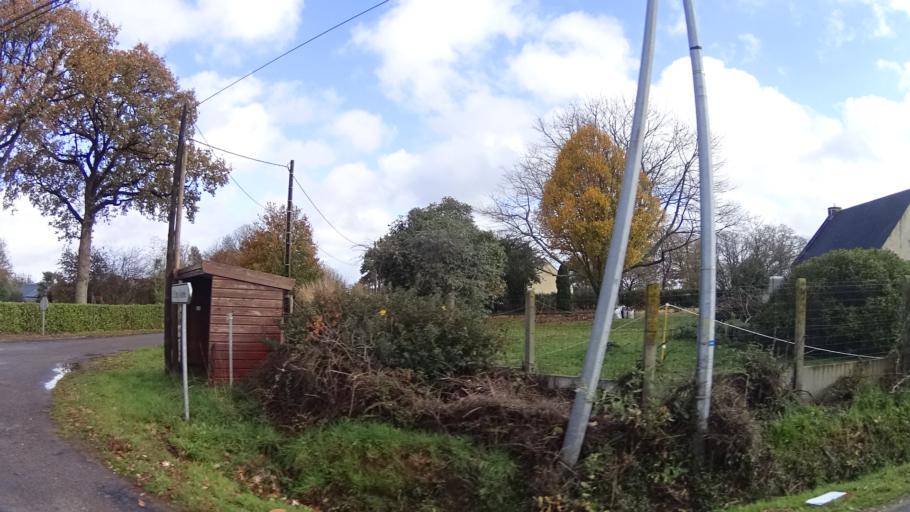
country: FR
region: Pays de la Loire
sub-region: Departement de la Loire-Atlantique
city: Saint-Nicolas-de-Redon
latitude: 47.6131
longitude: -2.0673
